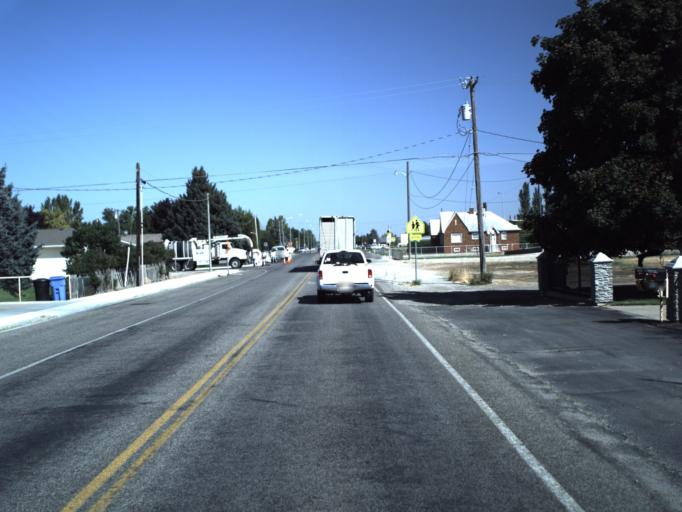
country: US
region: Utah
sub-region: Cache County
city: Hyrum
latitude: 41.6253
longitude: -111.8326
